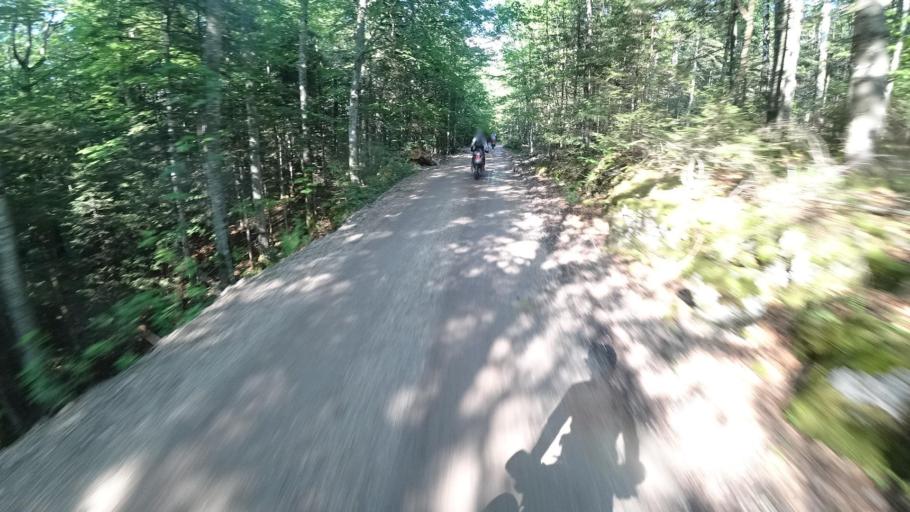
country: BA
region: Federation of Bosnia and Herzegovina
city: Sanica
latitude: 44.6779
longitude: 16.4910
